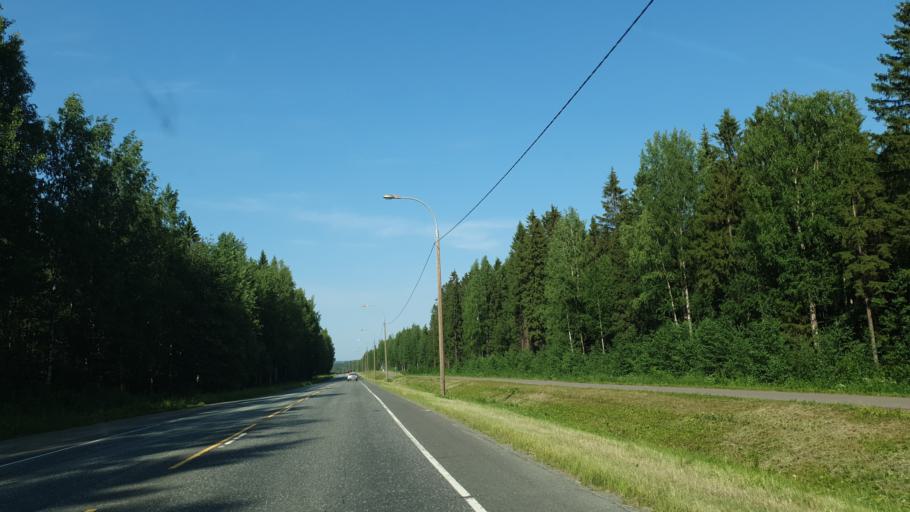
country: FI
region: Northern Savo
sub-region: Kuopio
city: Siilinjaervi
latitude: 63.1049
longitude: 27.7466
